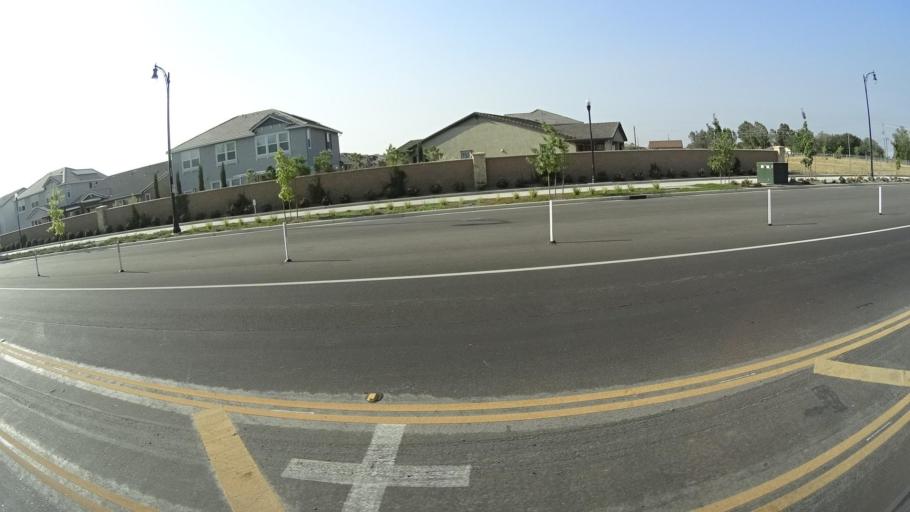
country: US
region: California
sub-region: Sacramento County
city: Laguna
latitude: 38.3796
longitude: -121.4156
